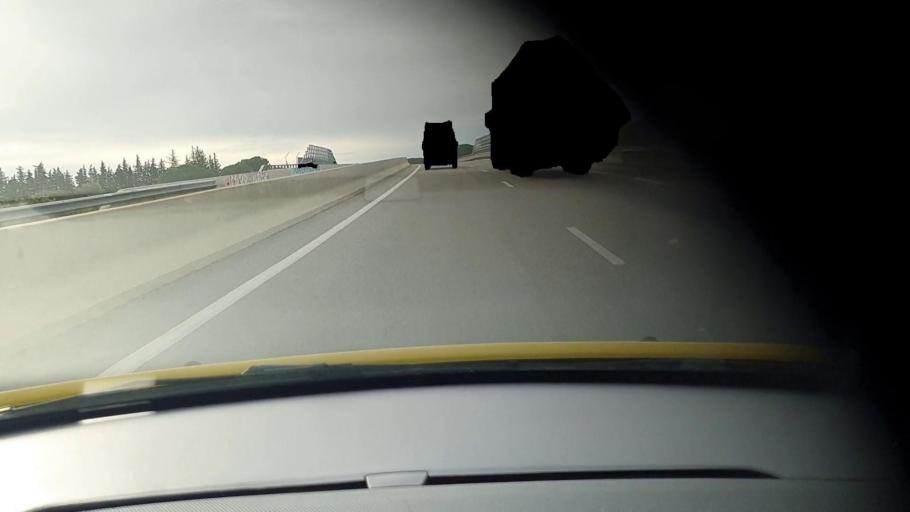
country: FR
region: Languedoc-Roussillon
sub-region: Departement du Gard
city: Caissargues
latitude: 43.7808
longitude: 4.3941
